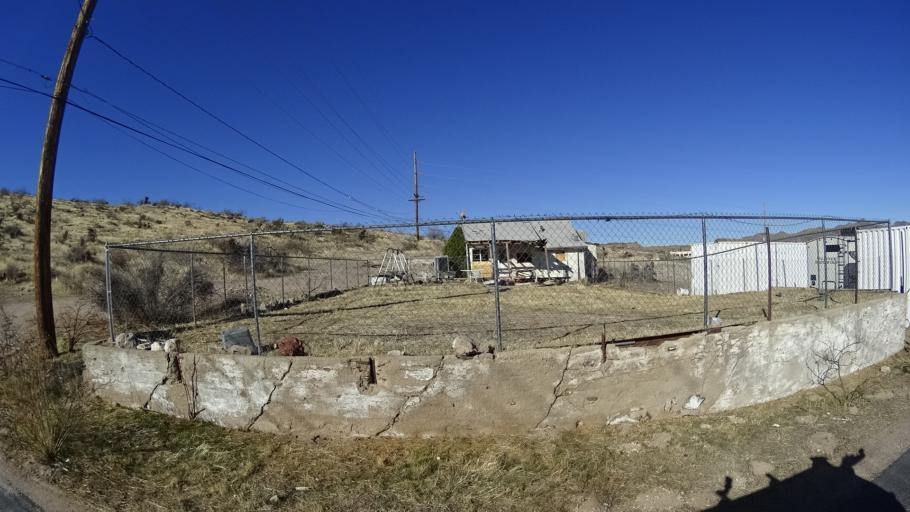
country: US
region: Arizona
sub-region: Mohave County
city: Kingman
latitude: 35.1854
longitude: -114.0592
